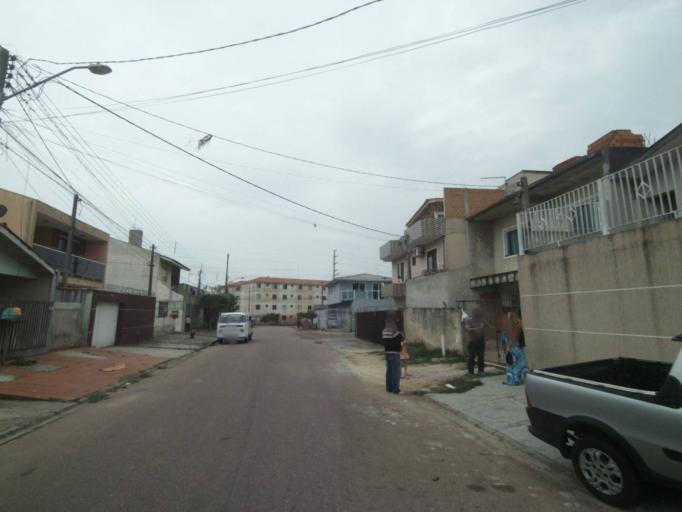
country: BR
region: Parana
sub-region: Sao Jose Dos Pinhais
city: Sao Jose dos Pinhais
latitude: -25.5477
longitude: -49.2673
